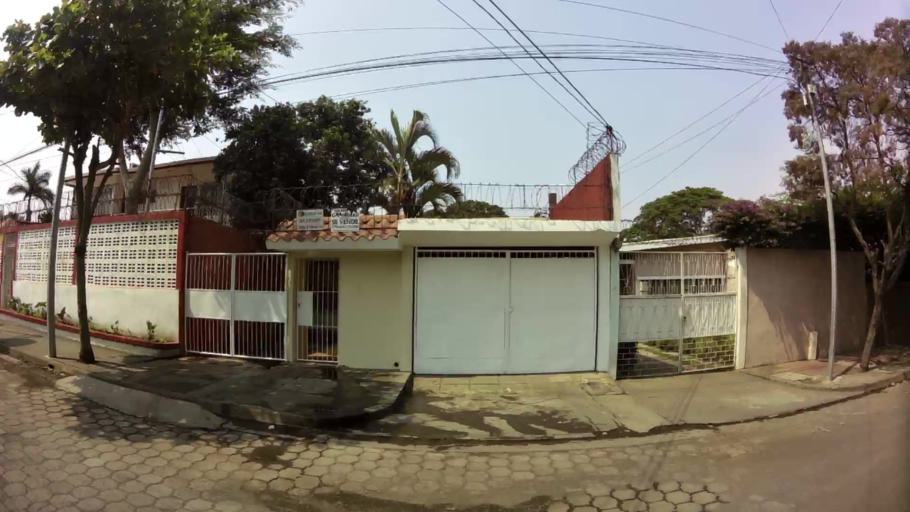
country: NI
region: Managua
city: Ciudad Sandino
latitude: 12.1266
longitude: -86.3131
